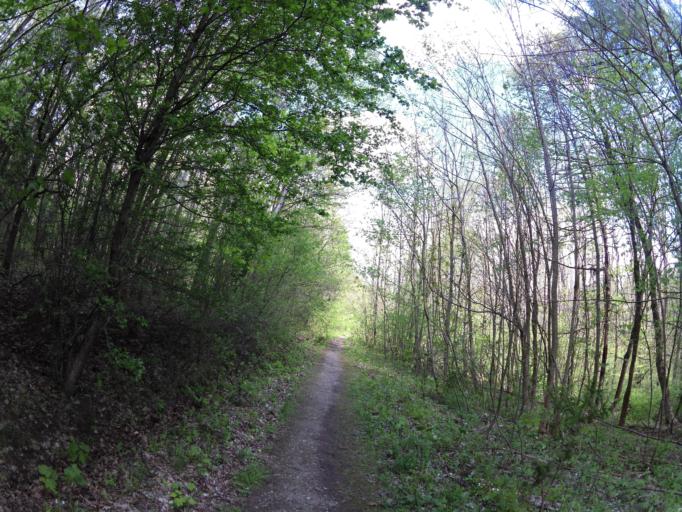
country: DE
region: Thuringia
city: Weberstedt
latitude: 51.0860
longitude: 10.4999
